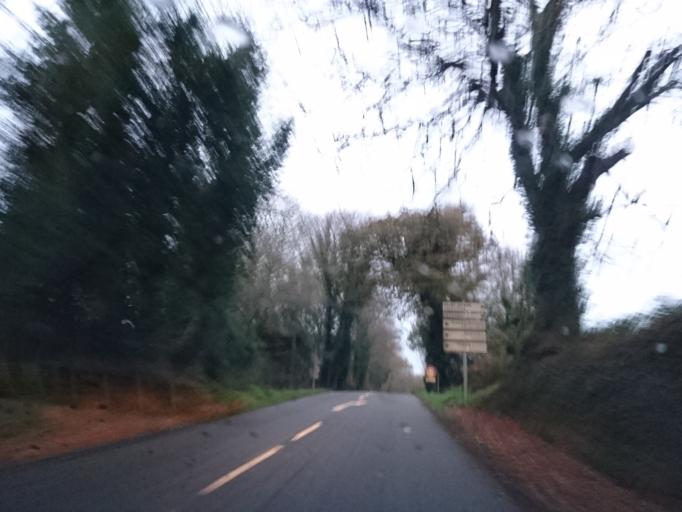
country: FR
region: Brittany
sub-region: Departement du Finistere
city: Le Conquet
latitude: 48.3622
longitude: -4.7478
